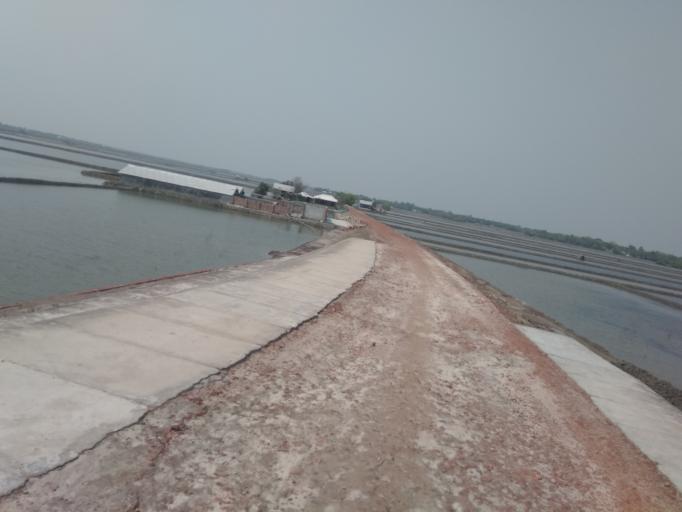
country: IN
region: West Bengal
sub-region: North 24 Parganas
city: Taki
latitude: 22.2896
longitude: 89.2734
